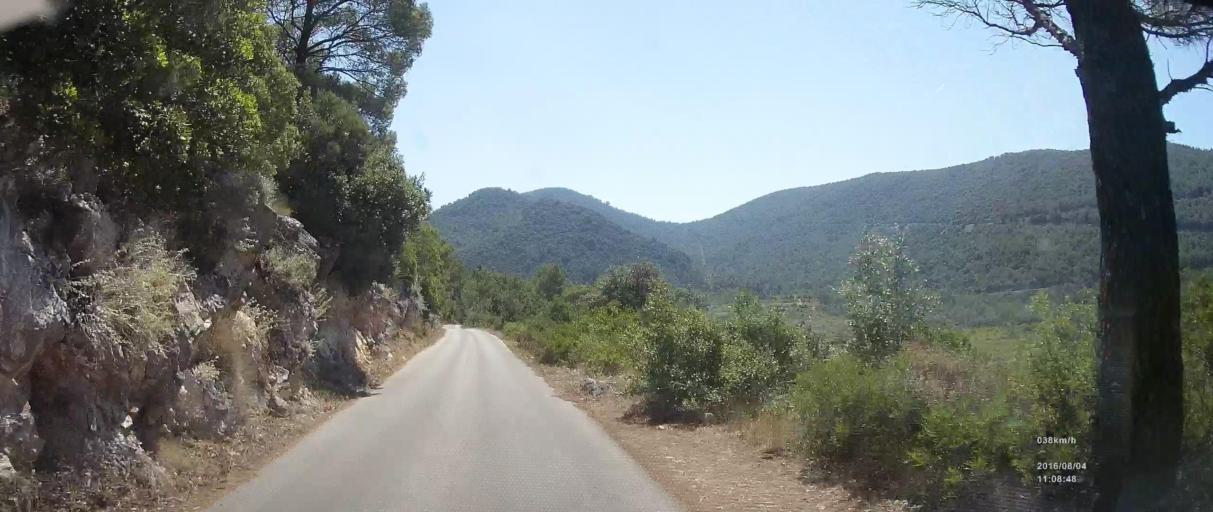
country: HR
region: Dubrovacko-Neretvanska
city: Blato
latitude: 42.7645
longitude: 17.4720
